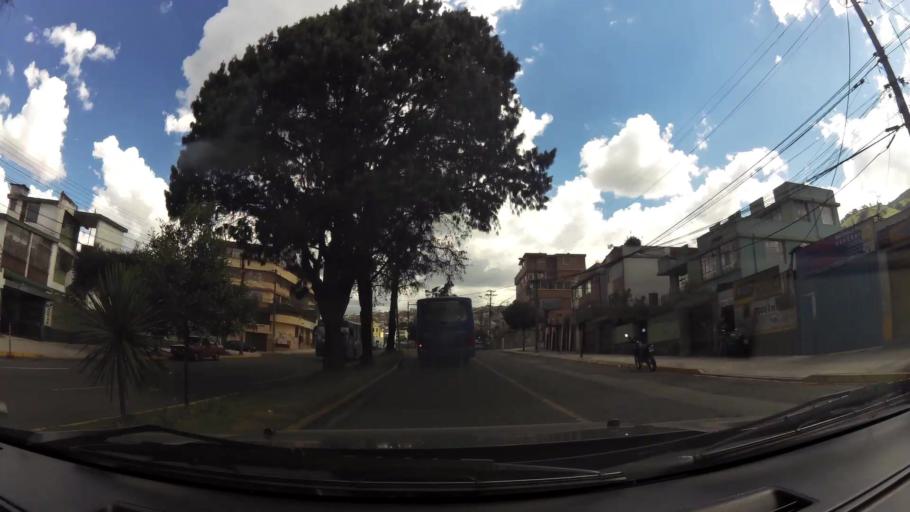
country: EC
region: Pichincha
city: Quito
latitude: -0.2034
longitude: -78.5049
